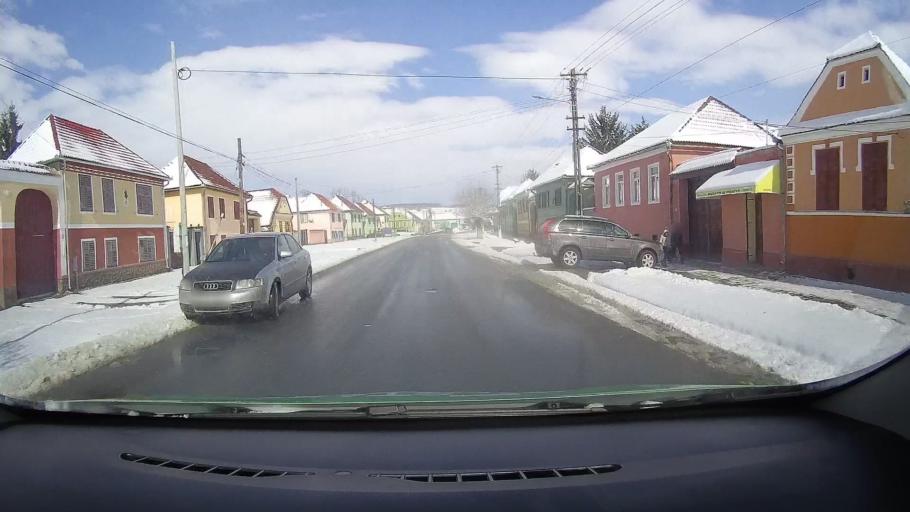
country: RO
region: Sibiu
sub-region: Comuna Altina
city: Altina
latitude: 45.9286
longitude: 24.4625
